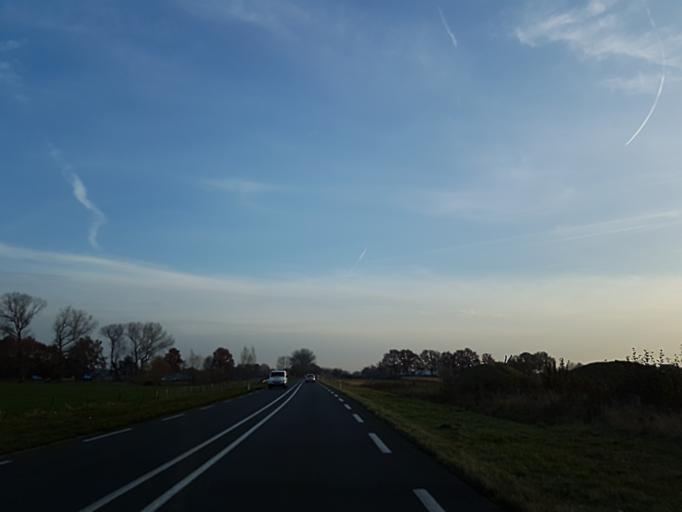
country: BE
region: Flanders
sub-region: Provincie Antwerpen
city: Essen
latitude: 51.4897
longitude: 4.4667
